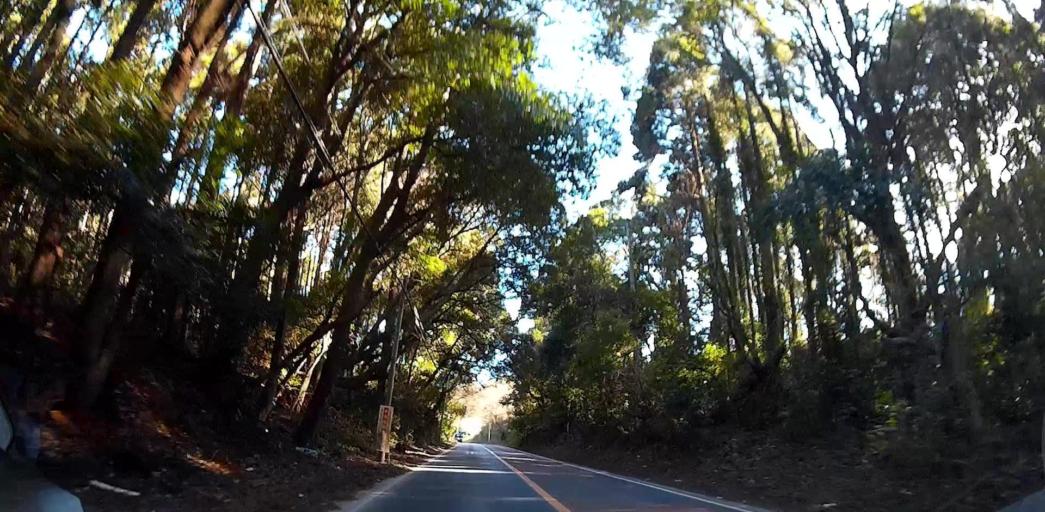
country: JP
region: Chiba
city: Yokaichiba
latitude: 35.7597
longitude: 140.4520
